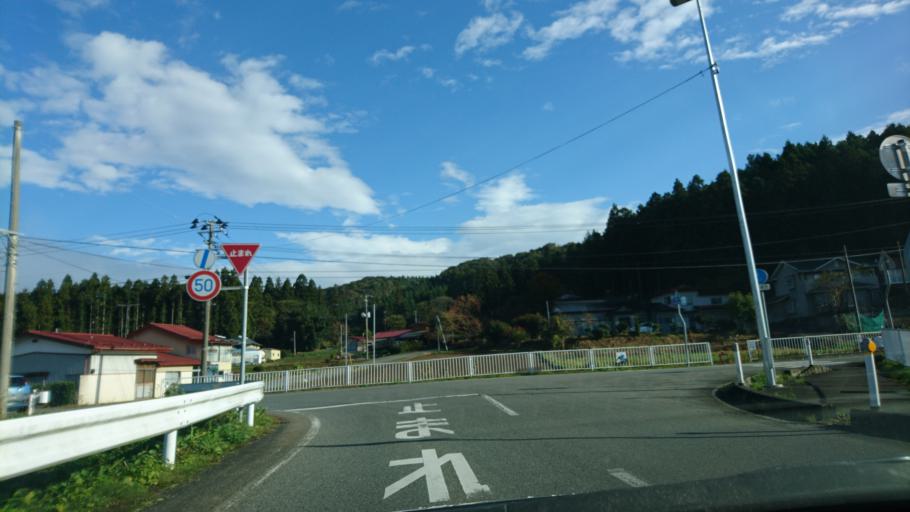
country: JP
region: Iwate
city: Mizusawa
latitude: 39.0429
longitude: 141.0611
